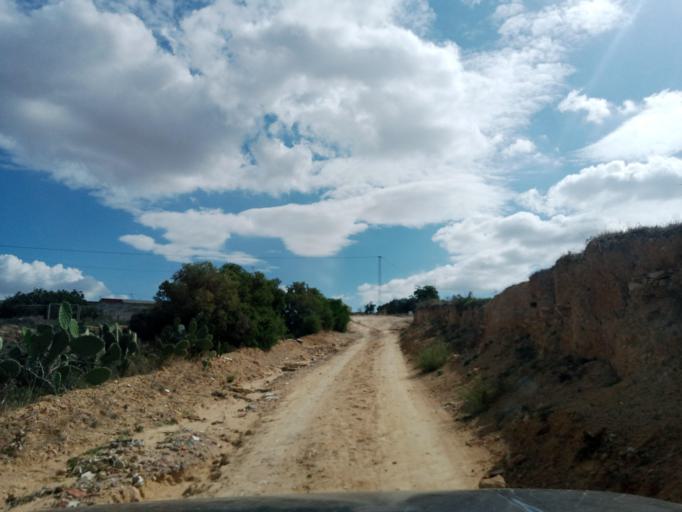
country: TN
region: Tunis
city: Oued Lill
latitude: 36.8107
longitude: 9.9813
